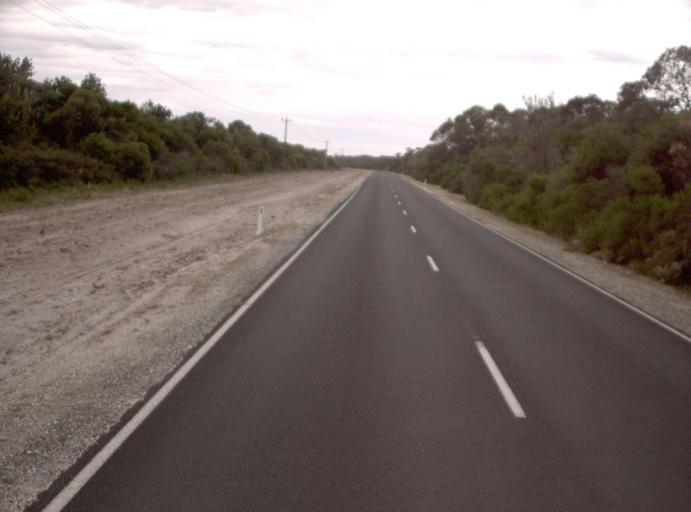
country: AU
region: Victoria
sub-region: East Gippsland
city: Bairnsdale
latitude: -38.0958
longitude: 147.5121
